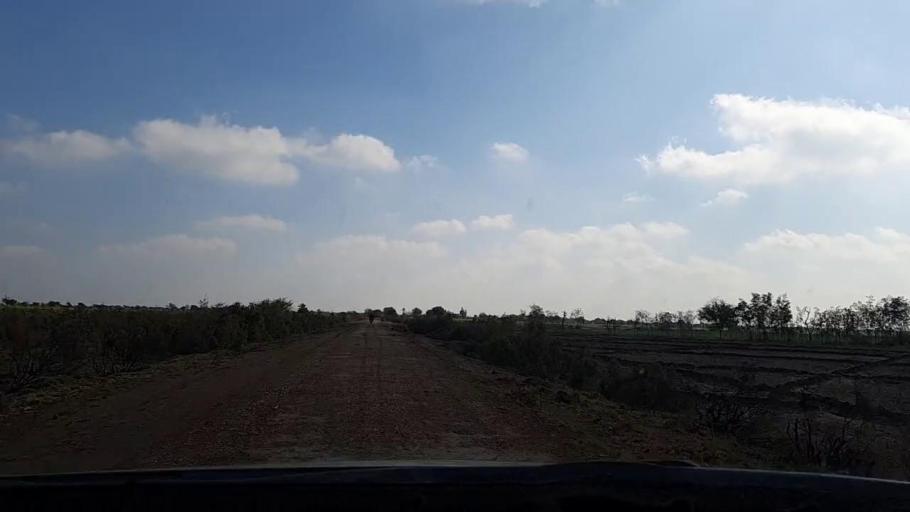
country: PK
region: Sindh
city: Pithoro
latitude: 25.7292
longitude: 69.2872
